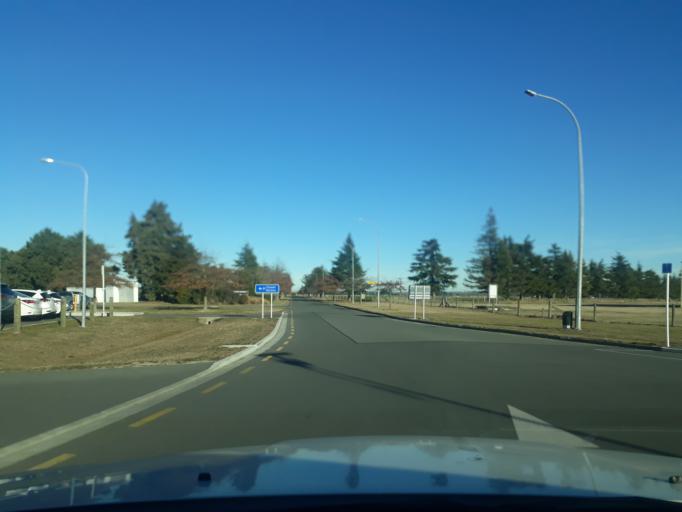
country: NZ
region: Canterbury
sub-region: Timaru District
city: Pleasant Point
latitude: -44.3035
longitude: 171.2254
